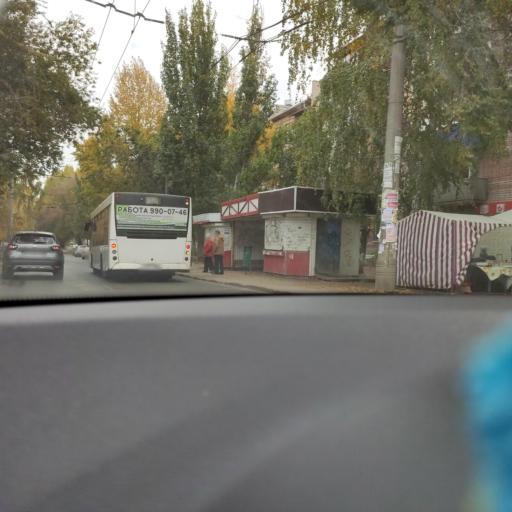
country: RU
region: Samara
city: Samara
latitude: 53.2163
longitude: 50.2367
